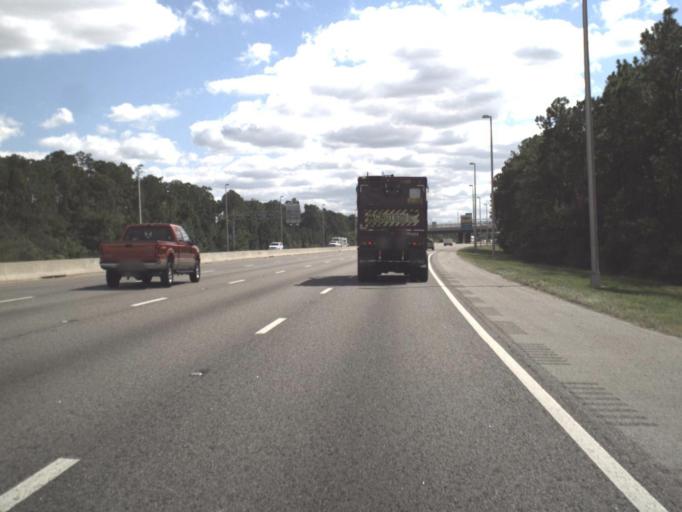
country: US
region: Florida
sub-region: Orange County
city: Oak Ridge
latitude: 28.4538
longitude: -81.4242
